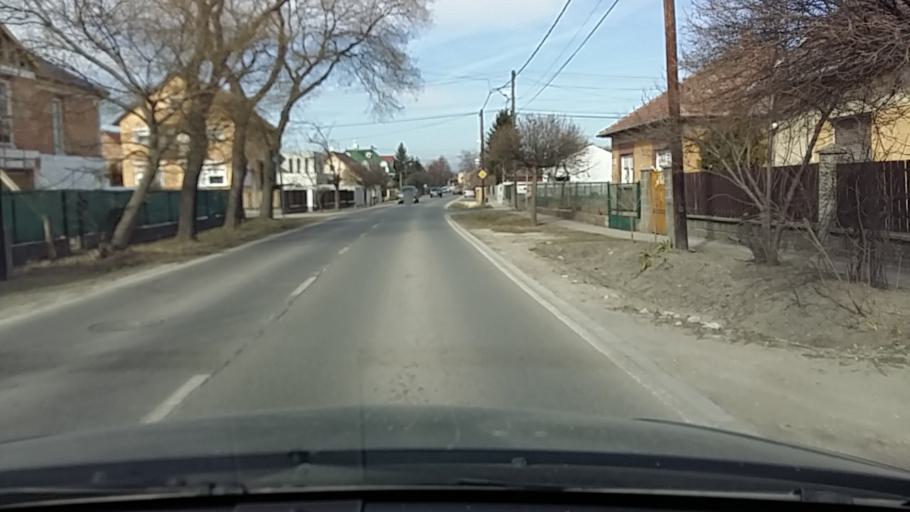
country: HU
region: Budapest
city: Budapest XXIII. keruelet
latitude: 47.4027
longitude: 19.0866
